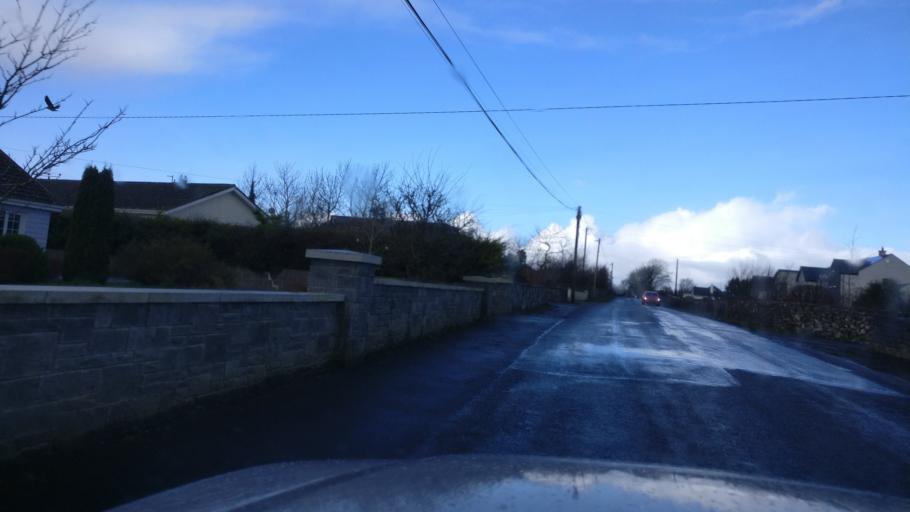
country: IE
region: Connaught
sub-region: County Galway
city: Oranmore
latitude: 53.2571
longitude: -8.8566
